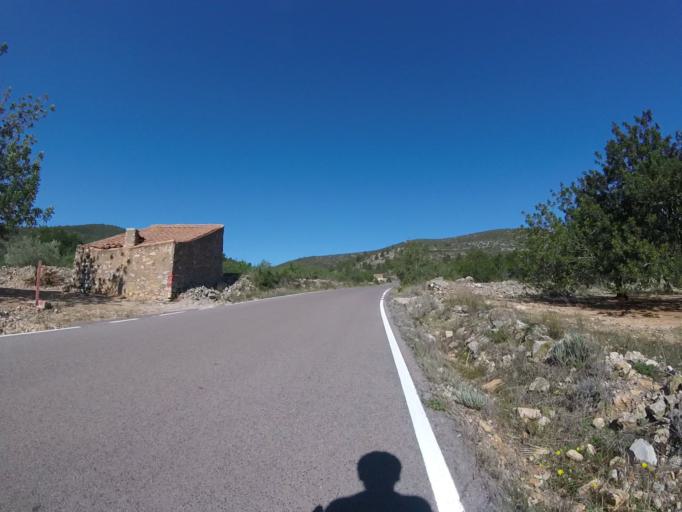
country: ES
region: Valencia
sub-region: Provincia de Castello
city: Santa Magdalena de Pulpis
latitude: 40.3822
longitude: 0.2626
